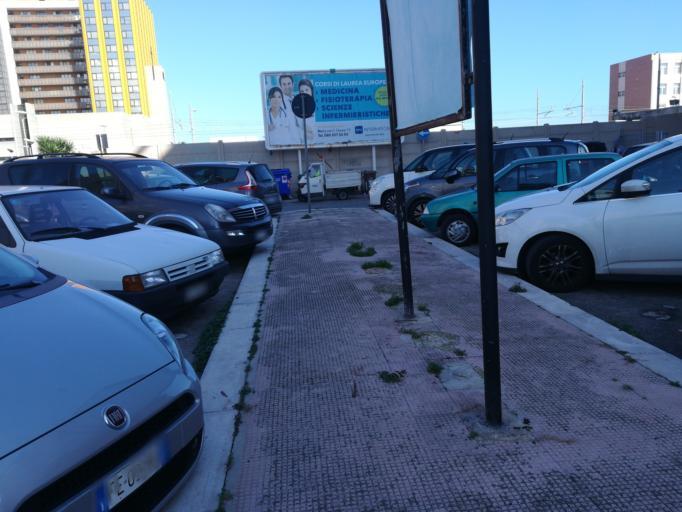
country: IT
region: Apulia
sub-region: Provincia di Bari
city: Bari
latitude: 41.1153
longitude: 16.8941
